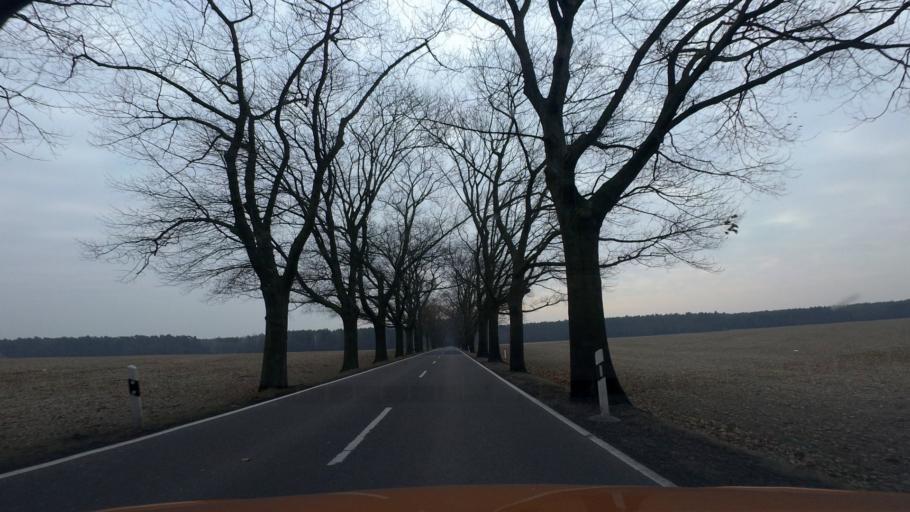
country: DE
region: Brandenburg
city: Ludwigsfelde
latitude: 52.2755
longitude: 13.2161
